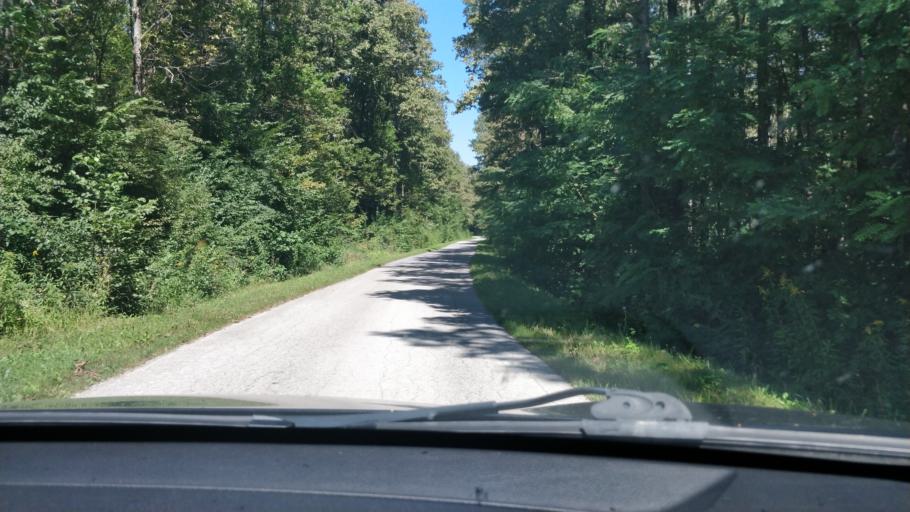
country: HR
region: Karlovacka
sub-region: Grad Karlovac
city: Karlovac
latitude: 45.4640
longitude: 15.6633
